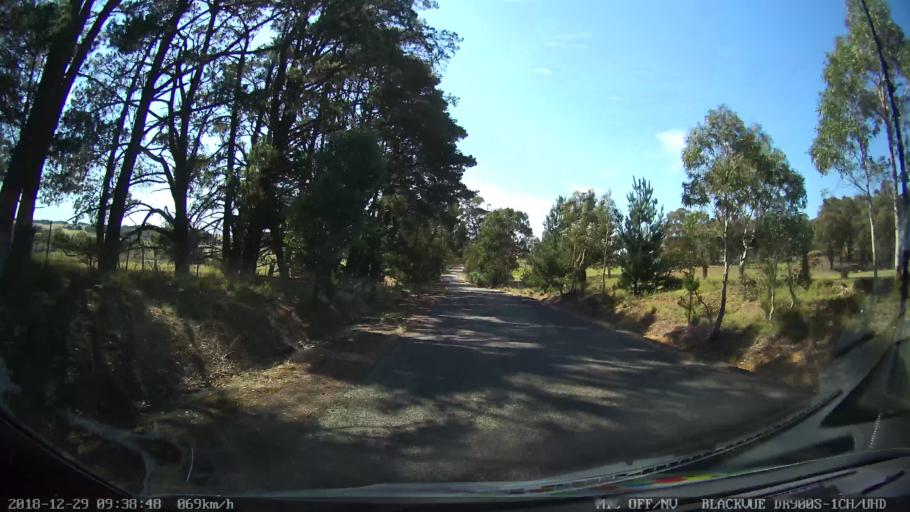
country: AU
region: New South Wales
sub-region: Upper Lachlan Shire
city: Crookwell
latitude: -34.6499
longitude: 149.3787
